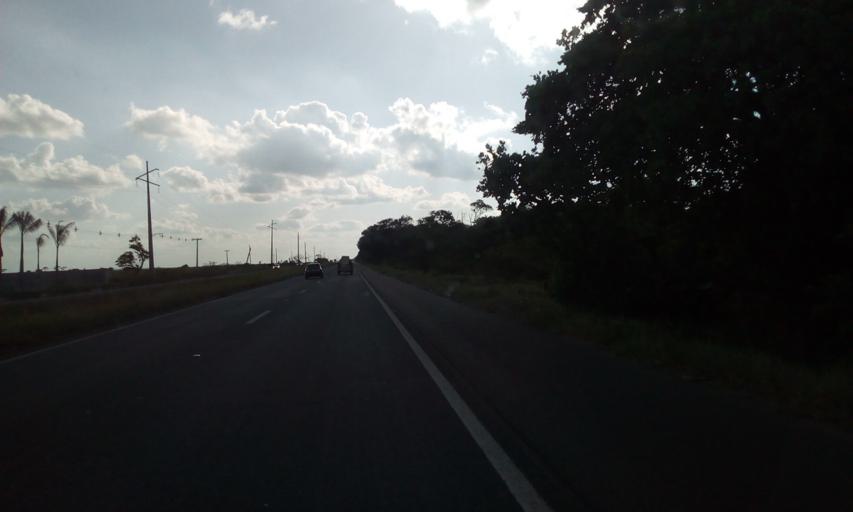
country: BR
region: Paraiba
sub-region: Santa Rita
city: Santa Rita
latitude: -7.1568
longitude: -35.0155
